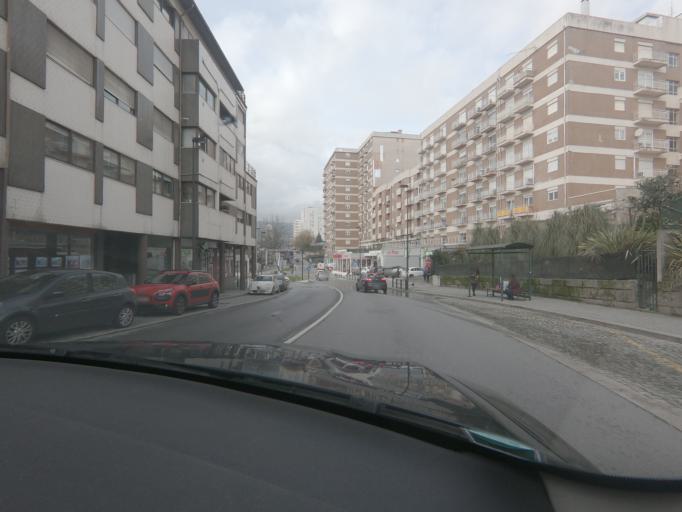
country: PT
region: Vila Real
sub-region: Vila Real
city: Vila Real
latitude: 41.2971
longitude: -7.7484
